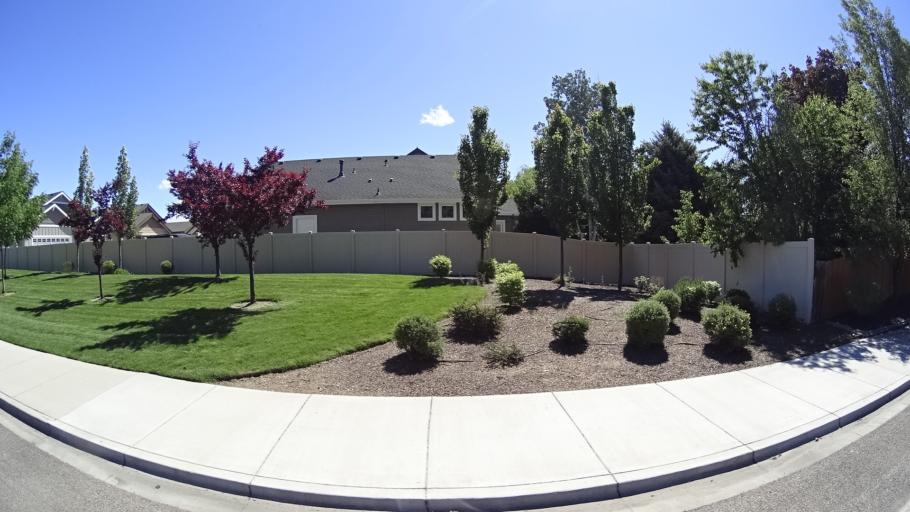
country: US
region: Idaho
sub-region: Ada County
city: Meridian
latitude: 43.6285
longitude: -116.3745
